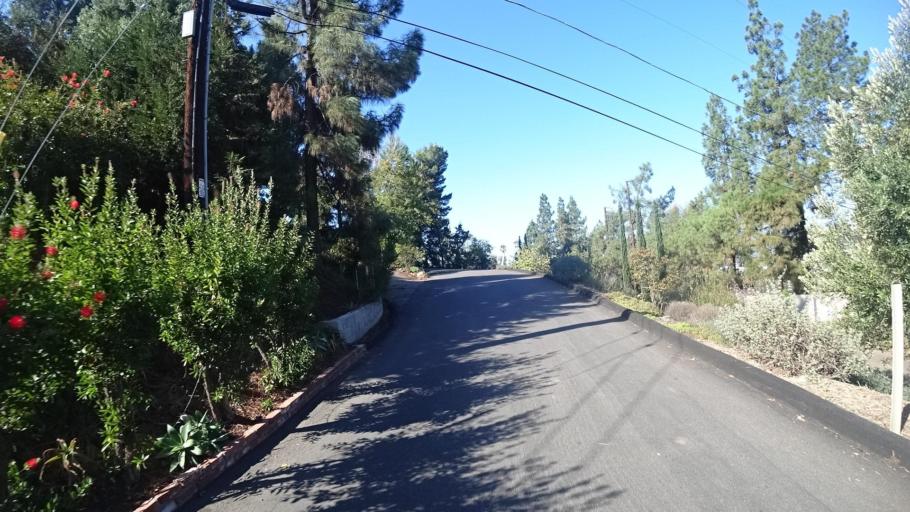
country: US
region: California
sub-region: San Diego County
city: Casa de Oro-Mount Helix
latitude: 32.7691
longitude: -116.9865
